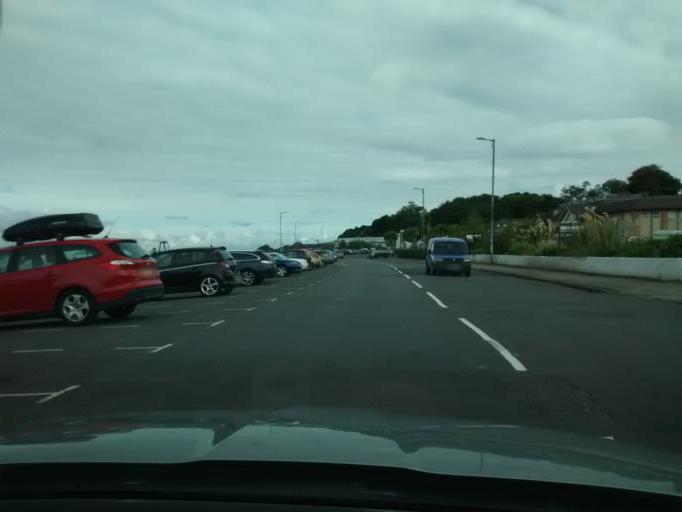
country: GB
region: Scotland
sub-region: North Ayrshire
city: Lamlash
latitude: 55.5769
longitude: -5.1443
